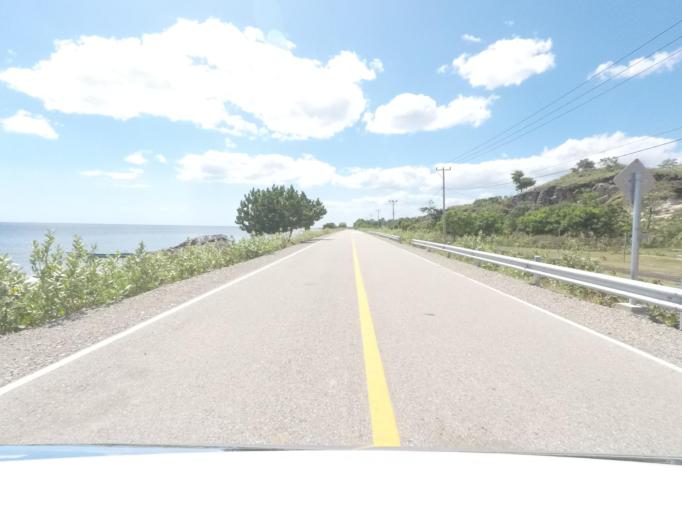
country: TL
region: Baucau
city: Baucau
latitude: -8.4493
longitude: 126.6415
